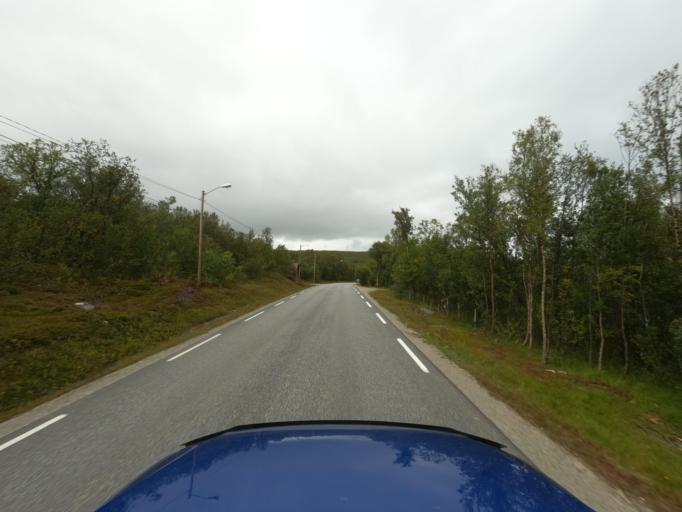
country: NO
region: Finnmark Fylke
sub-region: Porsanger
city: Lakselv
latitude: 70.3548
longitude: 25.0388
